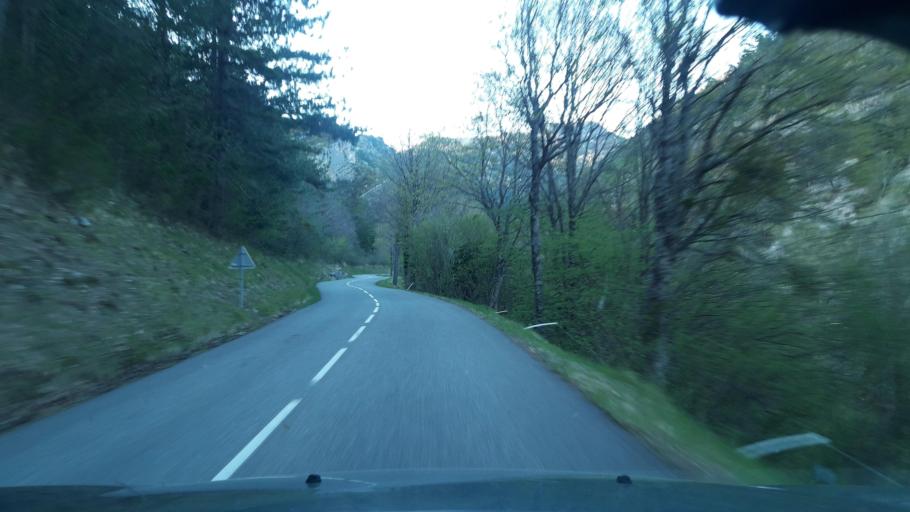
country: FR
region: Rhone-Alpes
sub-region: Departement de l'Isere
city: Mens
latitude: 44.6981
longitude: 5.6164
